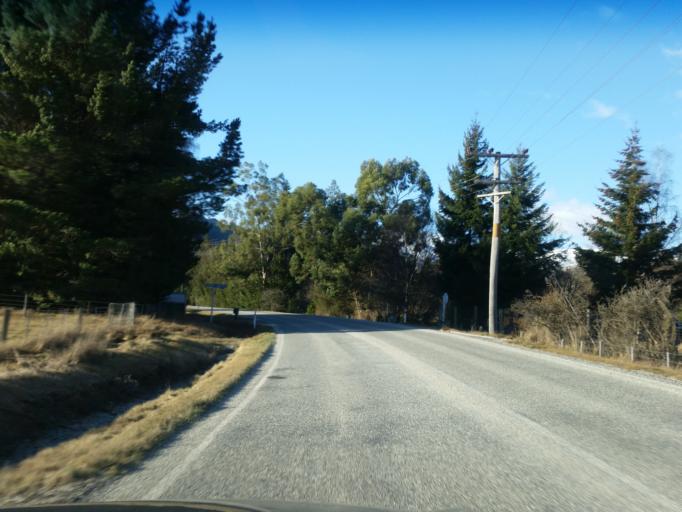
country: NZ
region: Otago
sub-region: Queenstown-Lakes District
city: Arrowtown
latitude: -44.9556
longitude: 168.7414
